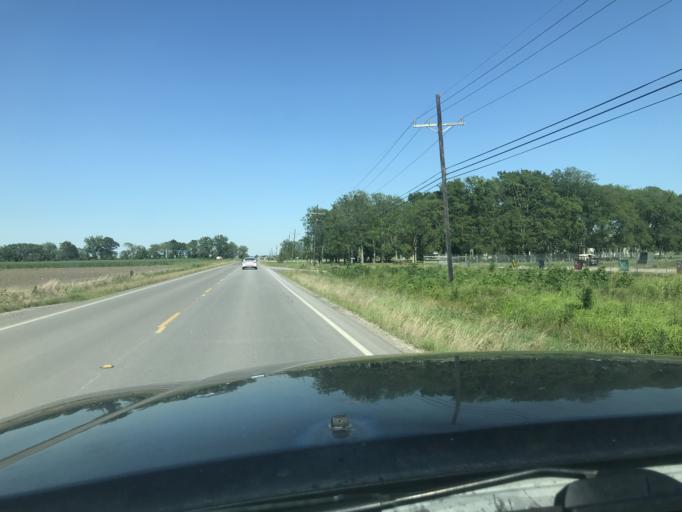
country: US
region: Louisiana
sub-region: West Baton Rouge Parish
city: Erwinville
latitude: 30.4688
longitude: -91.3275
